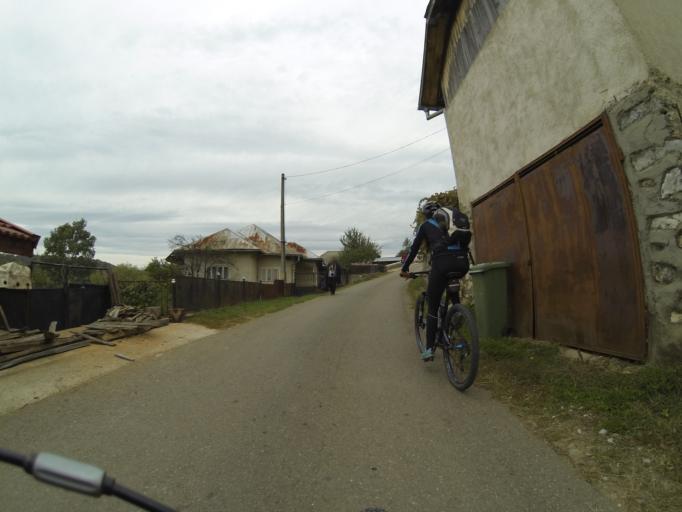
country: RO
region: Gorj
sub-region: Comuna Tismana
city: Sohodol
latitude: 45.0502
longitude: 22.8969
